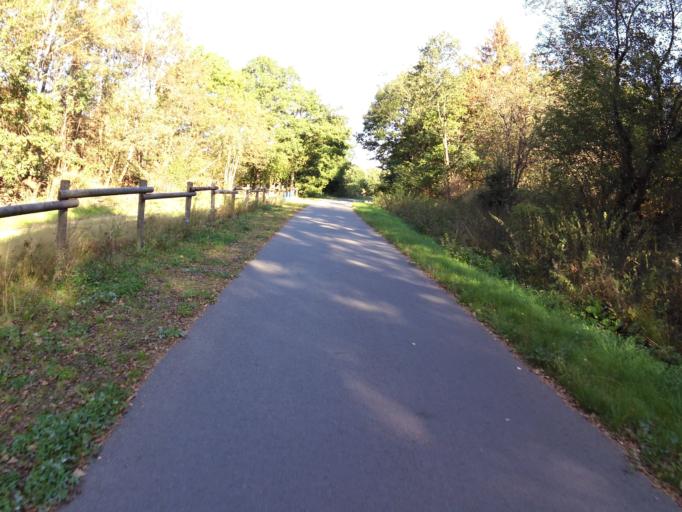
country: BE
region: Wallonia
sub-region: Province de Liege
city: Saint-Vith
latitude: 50.3287
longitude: 6.1199
